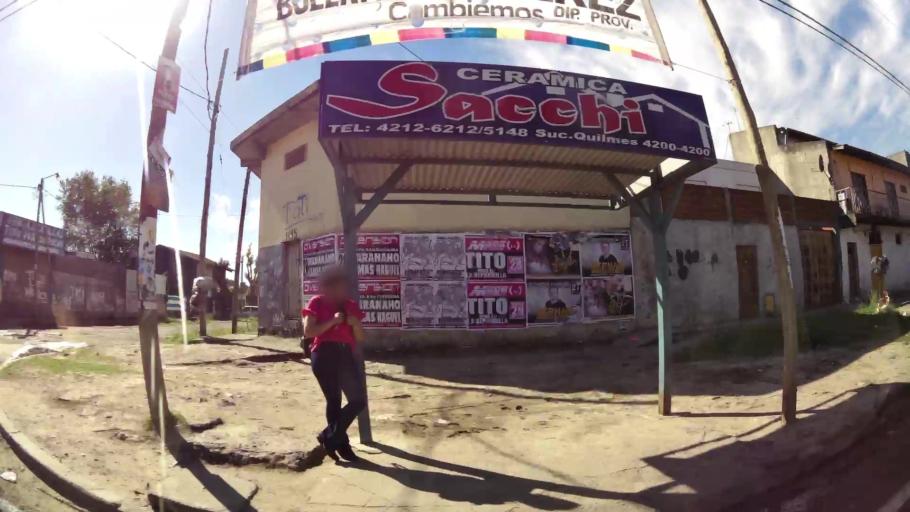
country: AR
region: Buenos Aires
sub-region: Partido de Quilmes
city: Quilmes
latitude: -34.7634
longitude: -58.3062
